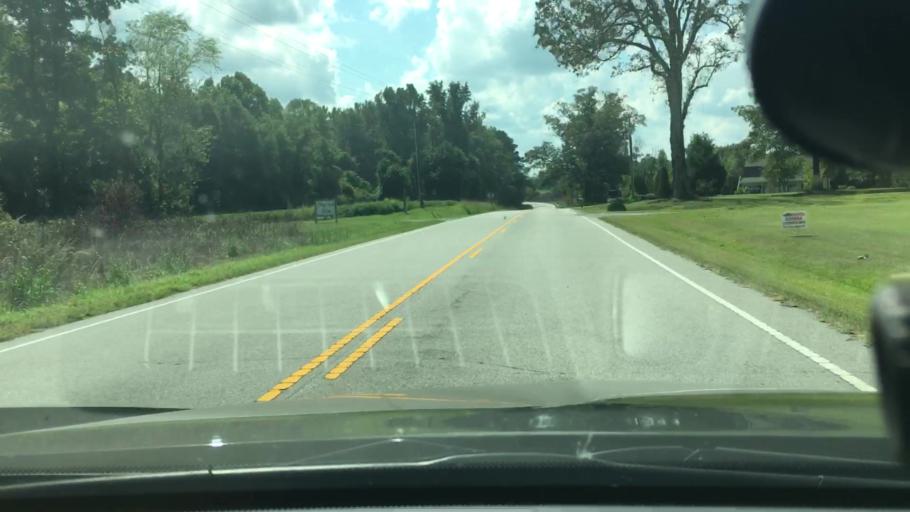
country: US
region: North Carolina
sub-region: Edgecombe County
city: Pinetops
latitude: 35.7445
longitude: -77.5404
